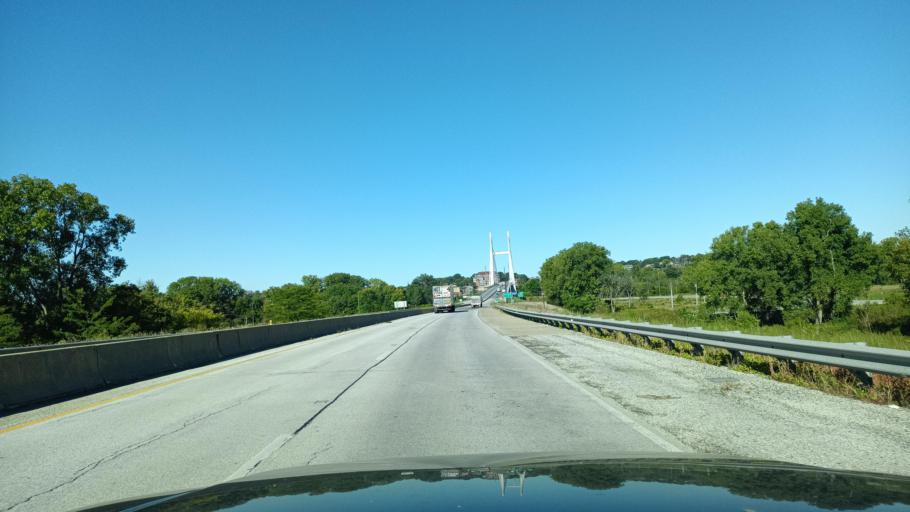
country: US
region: Iowa
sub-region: Des Moines County
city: Burlington
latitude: 40.8093
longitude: -91.0842
